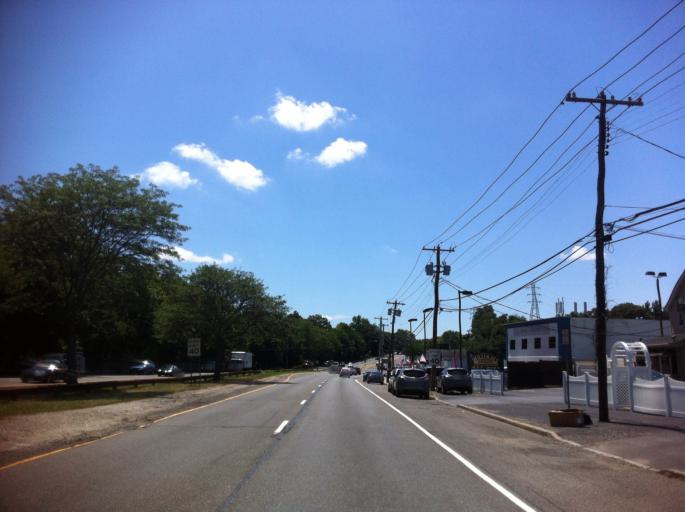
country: US
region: New York
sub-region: Nassau County
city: Greenvale
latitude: 40.8190
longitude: -73.6255
